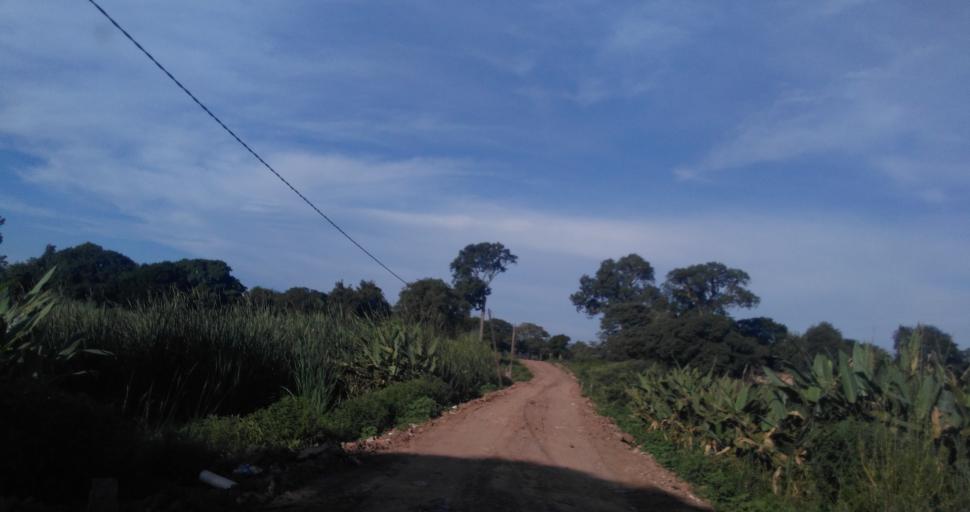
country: AR
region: Chaco
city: Fontana
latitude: -27.4107
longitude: -59.0241
